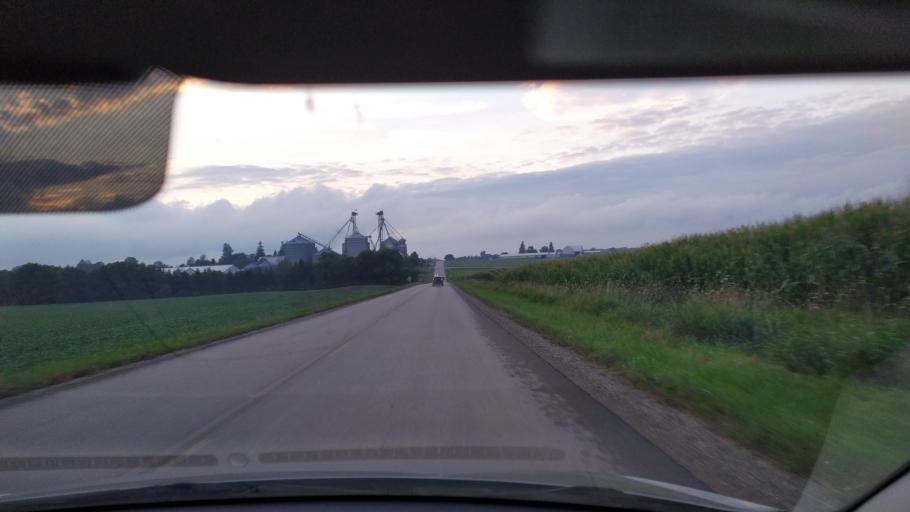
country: CA
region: Ontario
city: Kitchener
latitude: 43.3318
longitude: -80.6226
